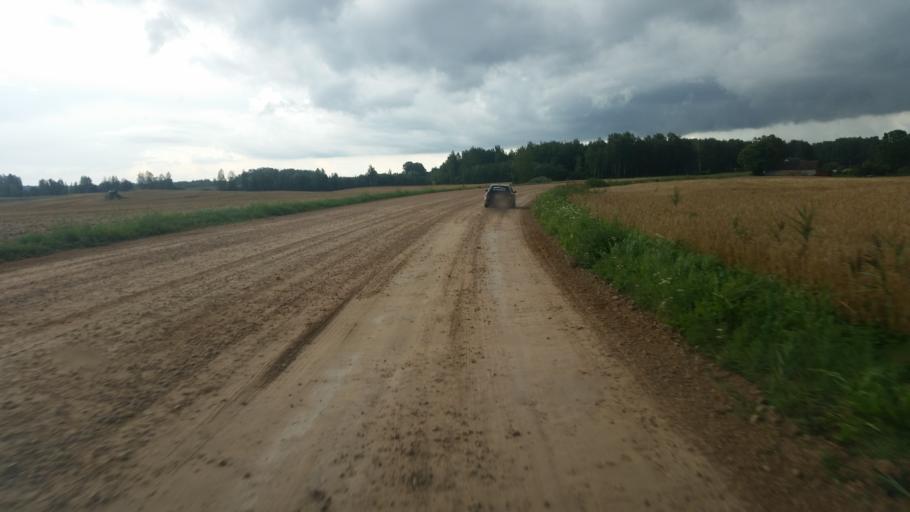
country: LV
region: Vecumnieki
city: Vecumnieki
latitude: 56.4261
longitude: 24.4876
